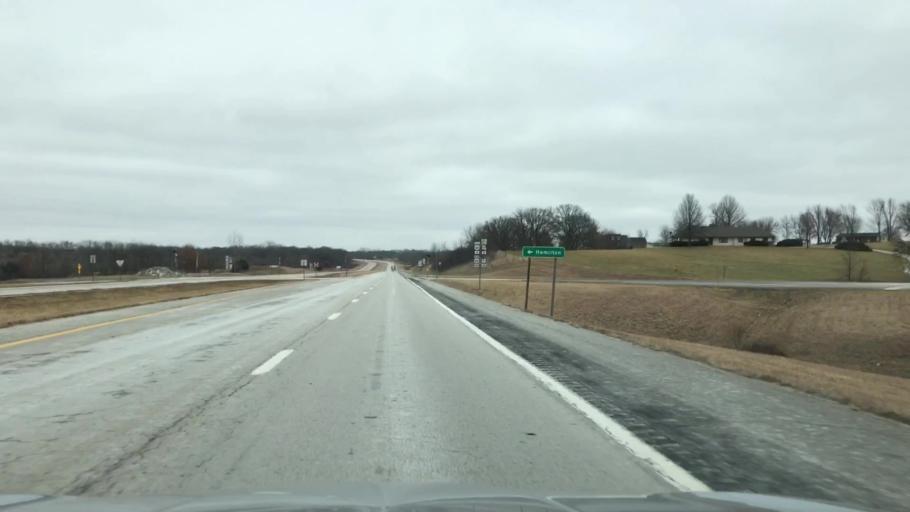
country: US
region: Missouri
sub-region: Caldwell County
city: Hamilton
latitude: 39.7422
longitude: -94.0392
